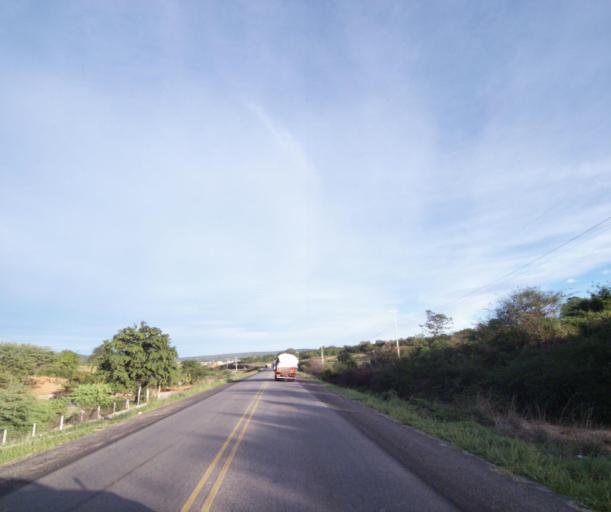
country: BR
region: Bahia
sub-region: Cacule
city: Cacule
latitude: -14.2016
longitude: -42.1314
